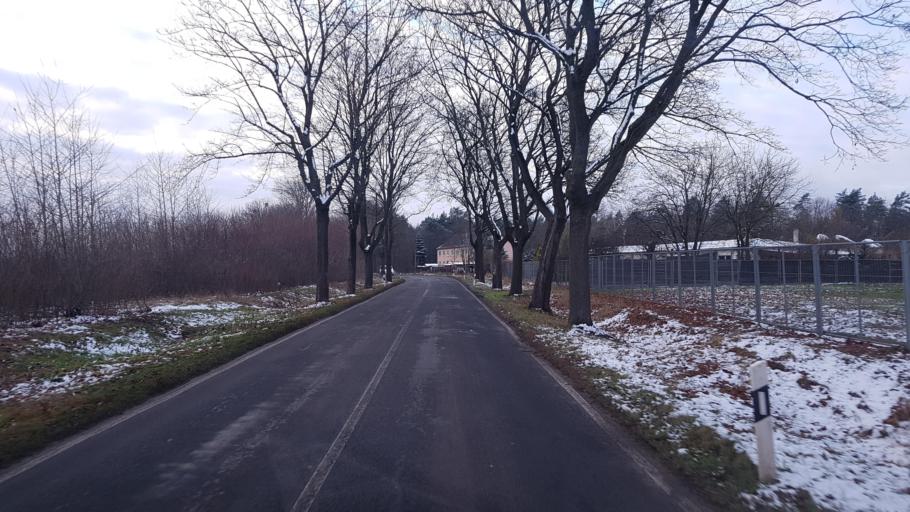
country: DE
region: Brandenburg
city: Rehfelde
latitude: 52.5101
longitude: 13.8781
